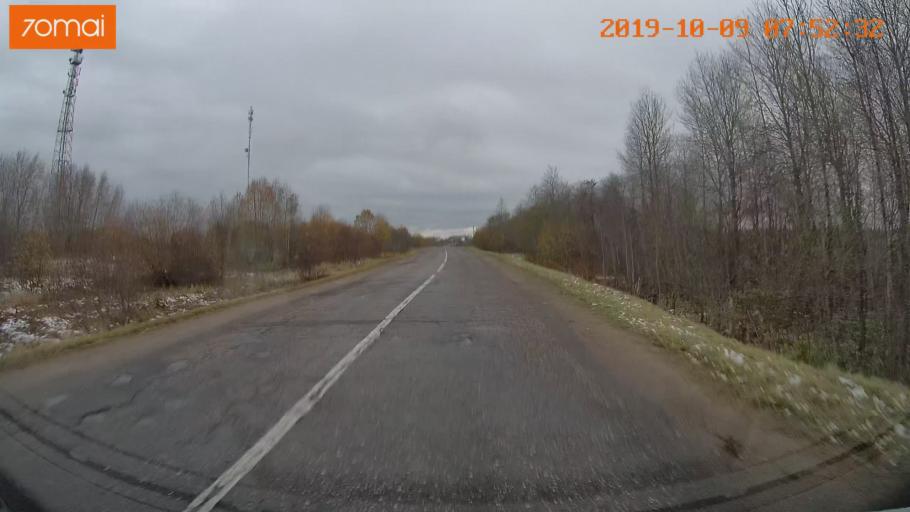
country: RU
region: Jaroslavl
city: Kukoboy
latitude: 58.6920
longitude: 39.8881
